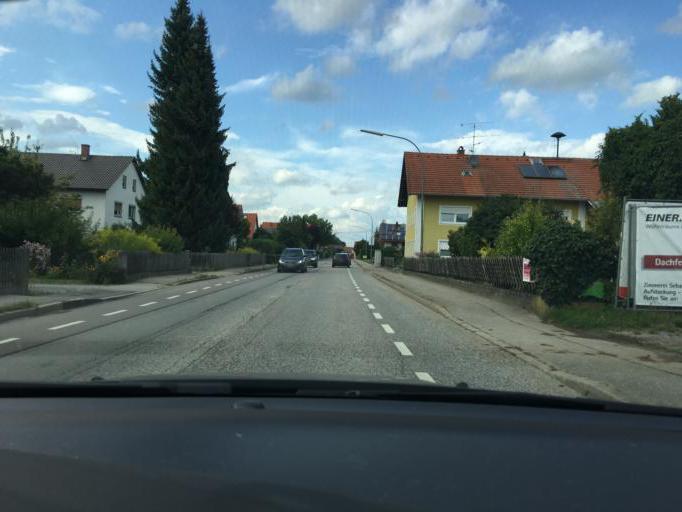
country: DE
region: Bavaria
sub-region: Upper Bavaria
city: Erding
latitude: 48.3211
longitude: 11.9240
